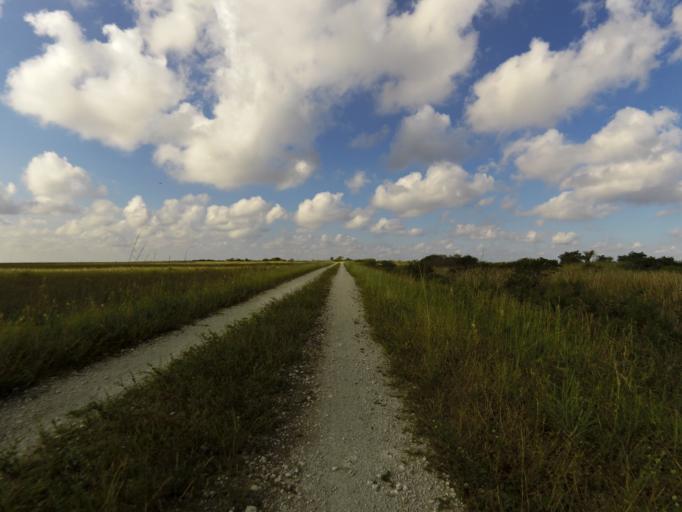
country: US
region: Florida
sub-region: Broward County
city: Weston
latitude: 26.0476
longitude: -80.4814
